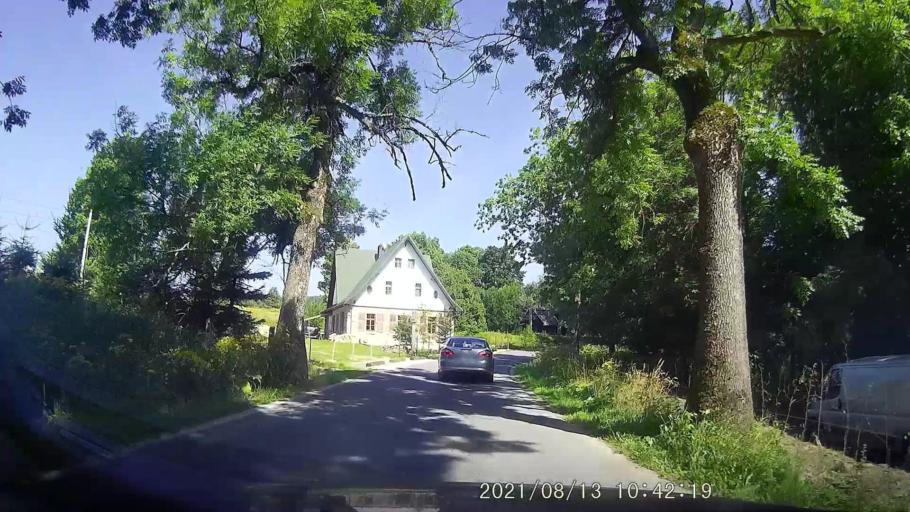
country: PL
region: Lower Silesian Voivodeship
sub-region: Powiat klodzki
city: Lewin Klodzki
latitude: 50.4568
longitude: 16.3410
